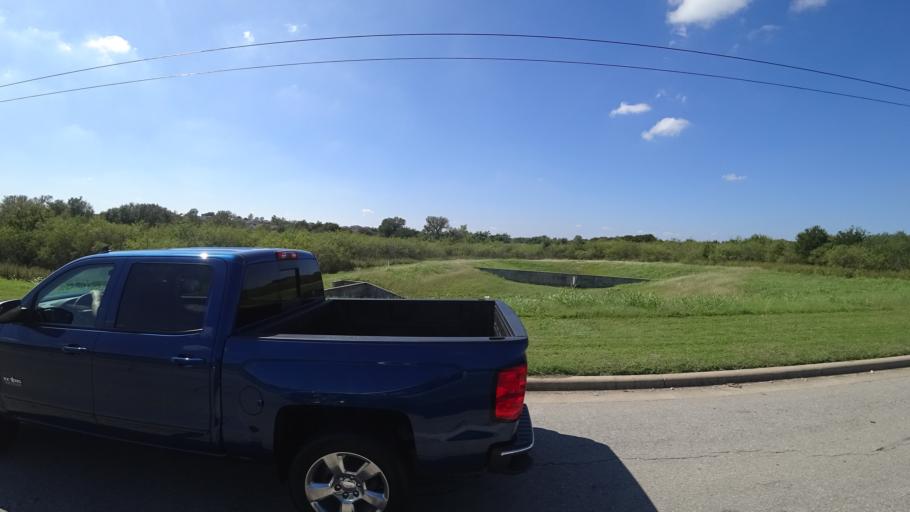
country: US
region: Texas
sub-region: Travis County
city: Manor
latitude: 30.3645
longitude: -97.6135
